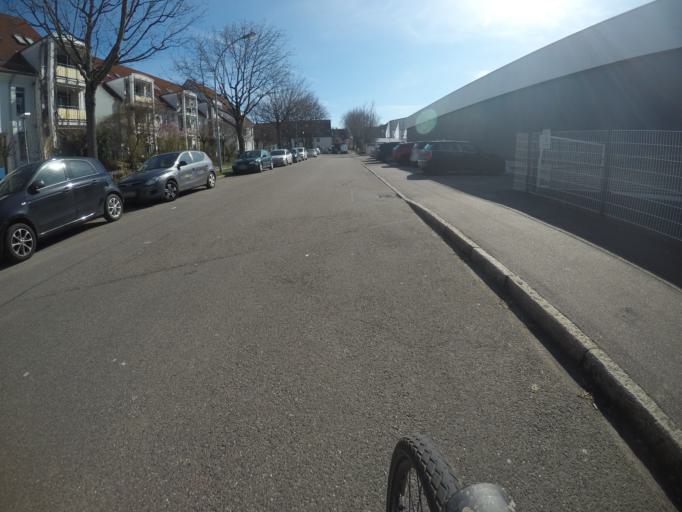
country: DE
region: Baden-Wuerttemberg
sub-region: Regierungsbezirk Stuttgart
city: Stuttgart Muehlhausen
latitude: 48.8409
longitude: 9.2581
